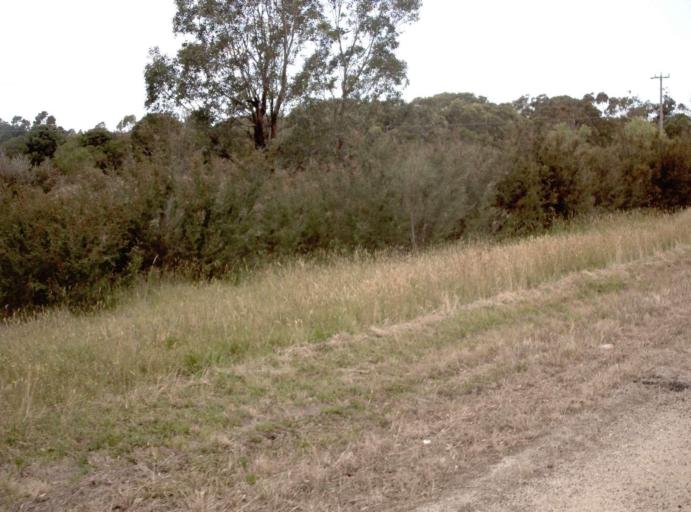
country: AU
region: Victoria
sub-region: Wellington
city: Sale
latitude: -38.1990
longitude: 147.0961
